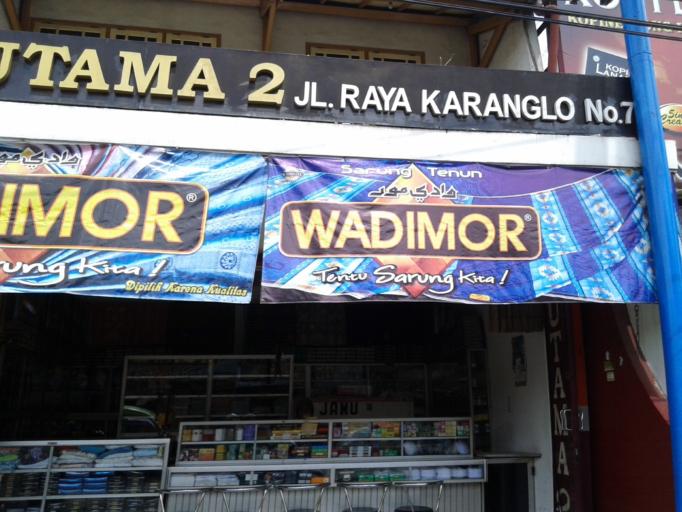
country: ID
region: East Java
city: Singosari
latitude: -7.9153
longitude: 112.6575
